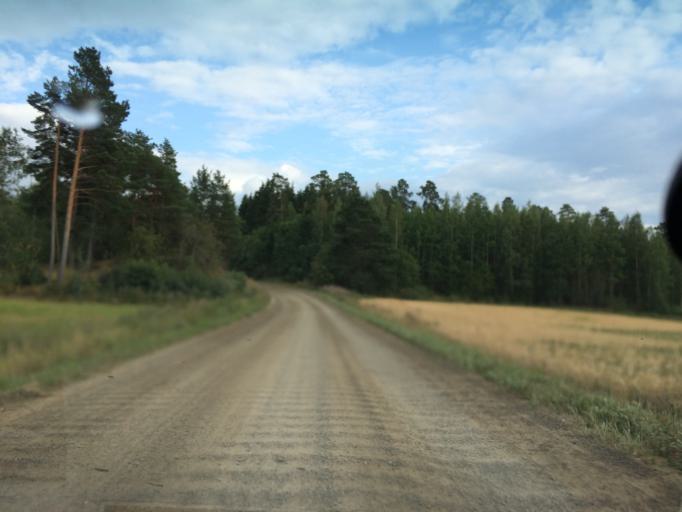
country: FI
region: Pirkanmaa
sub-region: Tampere
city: Luopioinen
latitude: 61.2628
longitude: 24.7012
